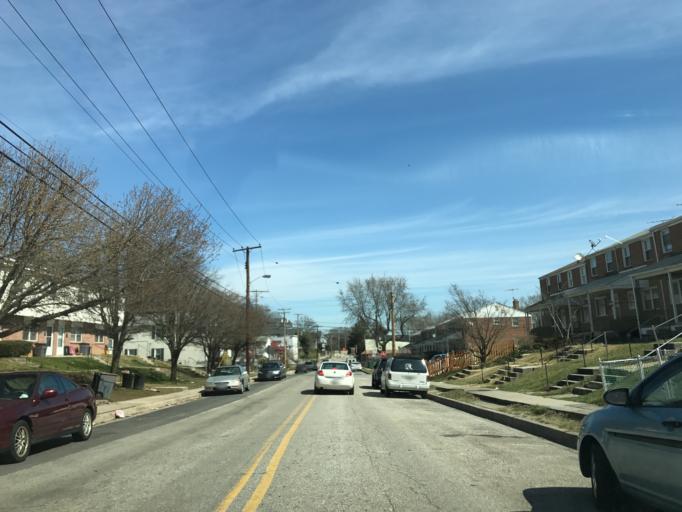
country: US
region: Maryland
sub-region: Baltimore County
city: Lansdowne
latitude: 39.2631
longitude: -76.6625
